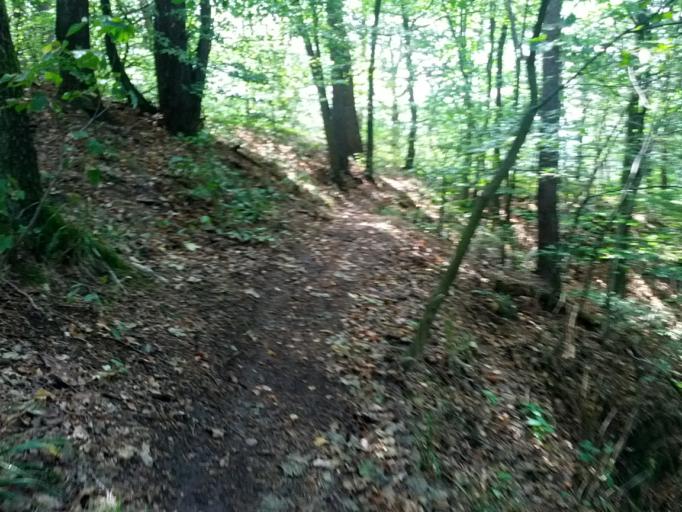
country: DE
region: Thuringia
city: Eisenach
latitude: 50.9577
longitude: 10.3166
